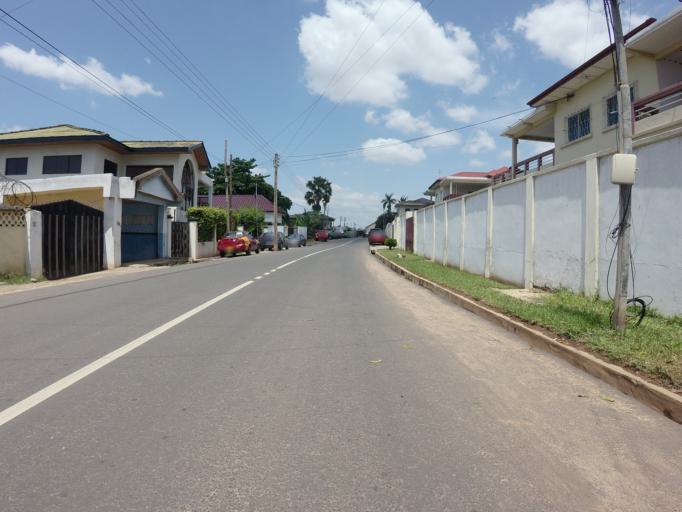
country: GH
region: Greater Accra
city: Accra
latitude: 5.5760
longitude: -0.2029
